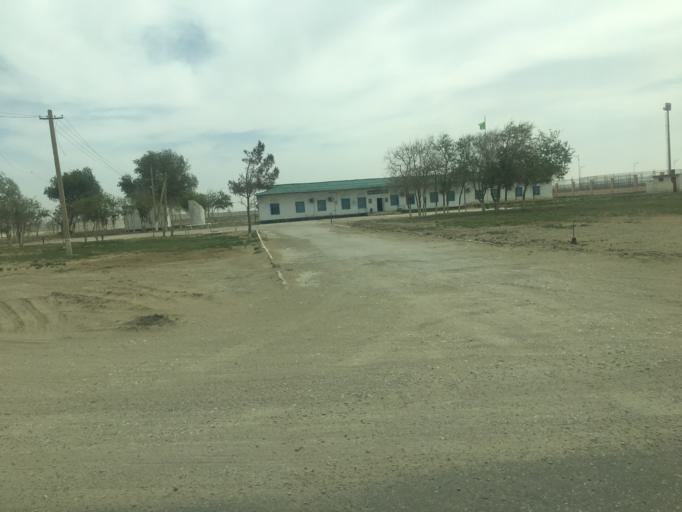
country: TM
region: Balkan
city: Turkmenbasy
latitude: 39.4098
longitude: 53.1352
